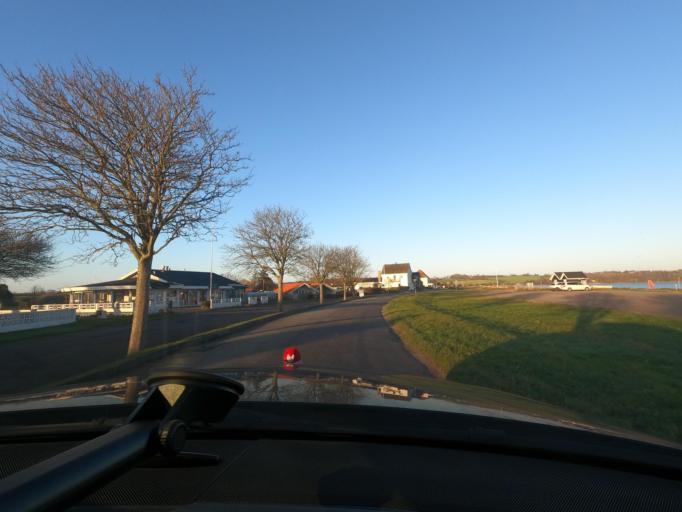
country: DK
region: South Denmark
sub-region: Sonderborg Kommune
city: Broager
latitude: 54.8948
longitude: 9.7003
